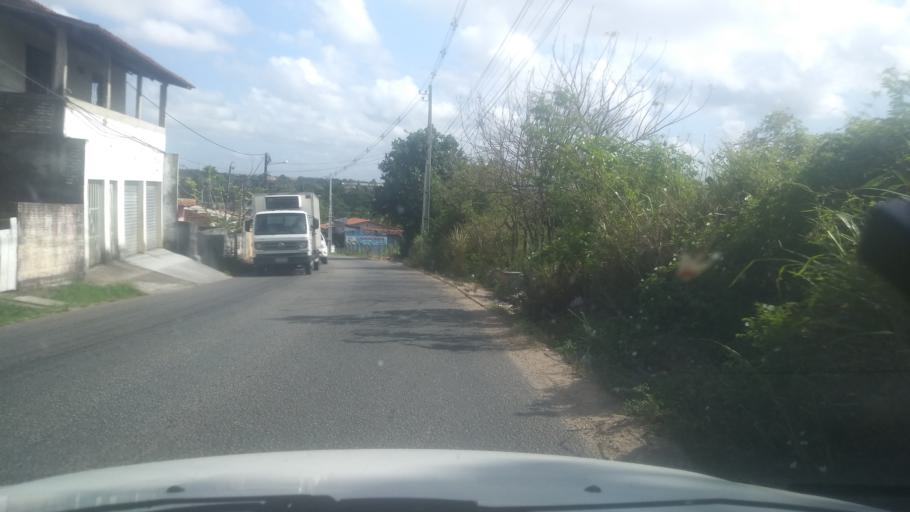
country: BR
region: Rio Grande do Norte
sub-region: Extremoz
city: Extremoz
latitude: -5.7106
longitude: -35.2777
